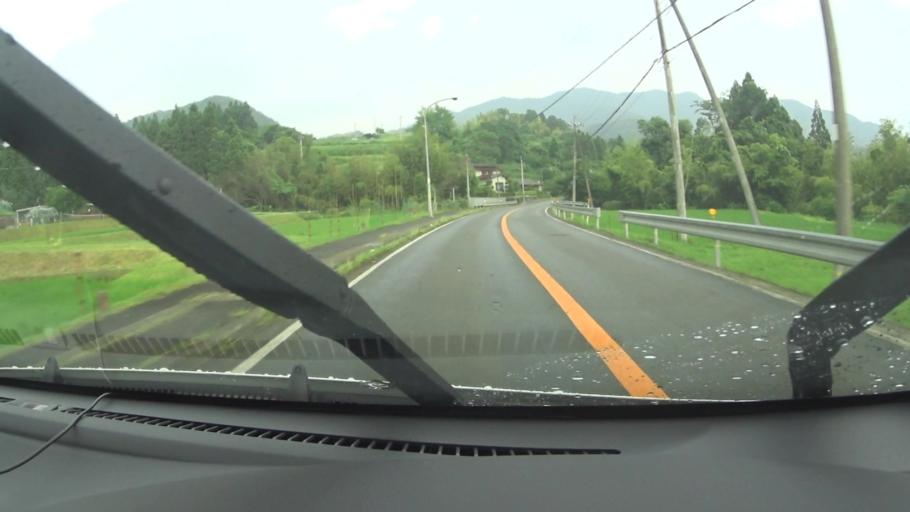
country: JP
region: Kyoto
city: Ayabe
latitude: 35.2980
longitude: 135.3254
